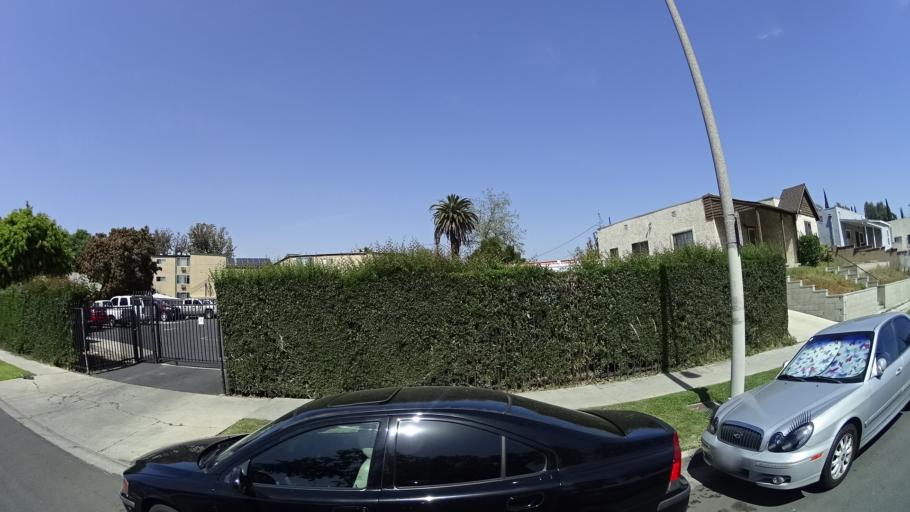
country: US
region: California
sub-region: Los Angeles County
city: Boyle Heights
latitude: 34.0524
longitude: -118.1966
